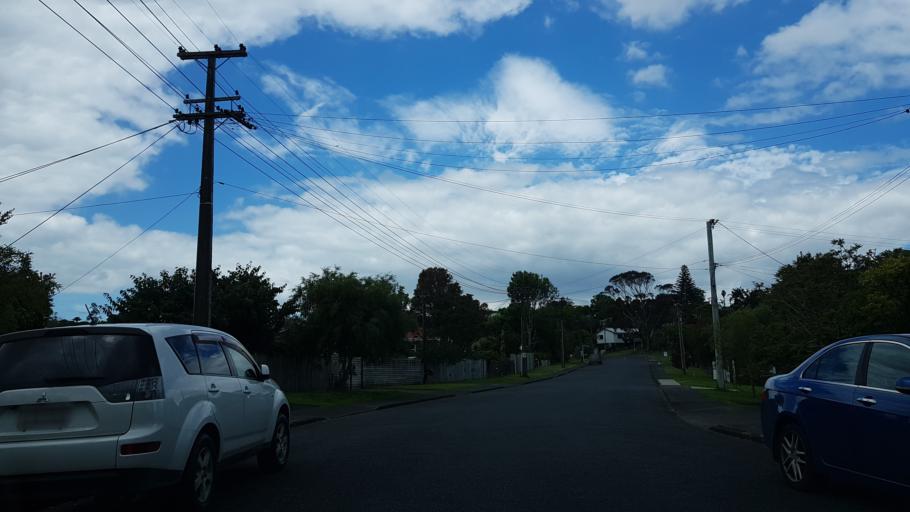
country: NZ
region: Auckland
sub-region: Auckland
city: North Shore
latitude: -36.7960
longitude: 174.6870
